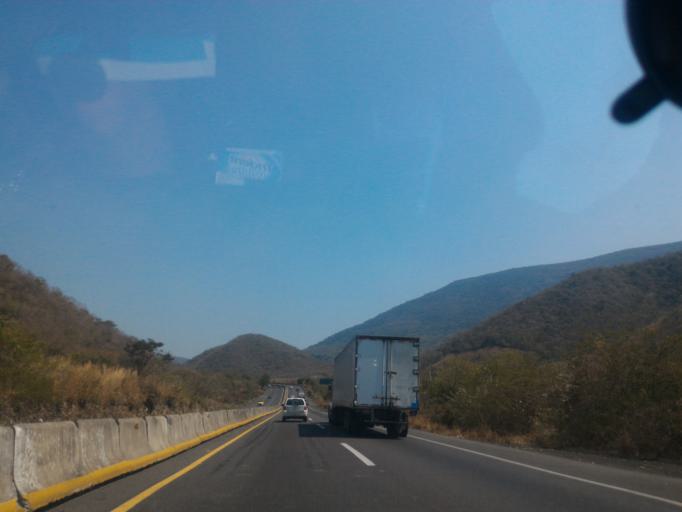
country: MX
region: Colima
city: Ixtlahuacan
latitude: 19.0227
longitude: -103.8118
